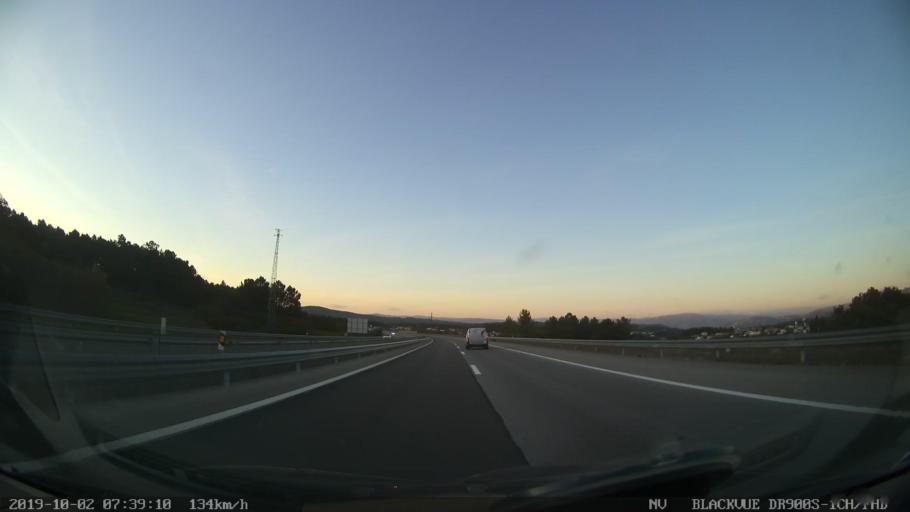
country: PT
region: Vila Real
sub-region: Vila Real
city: Vila Real
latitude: 41.2857
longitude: -7.6912
